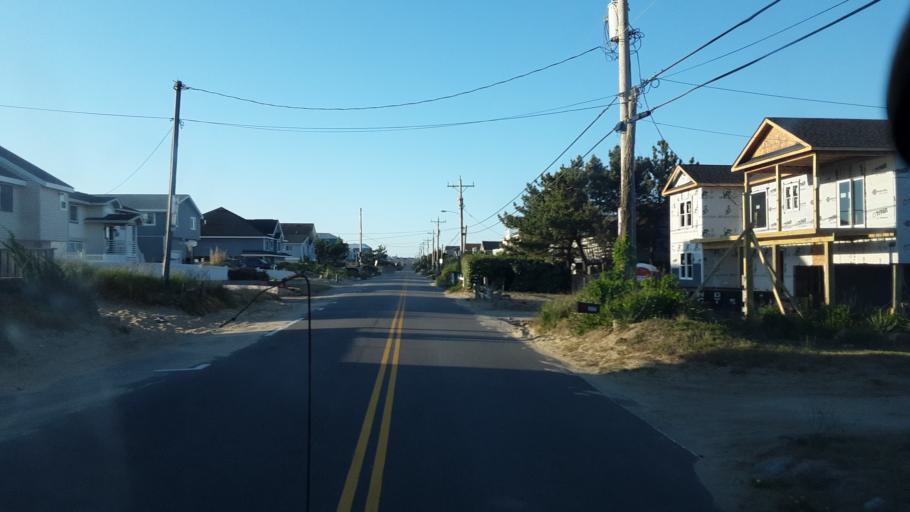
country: US
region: Virginia
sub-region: City of Virginia Beach
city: Virginia Beach
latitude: 36.7113
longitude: -75.9312
